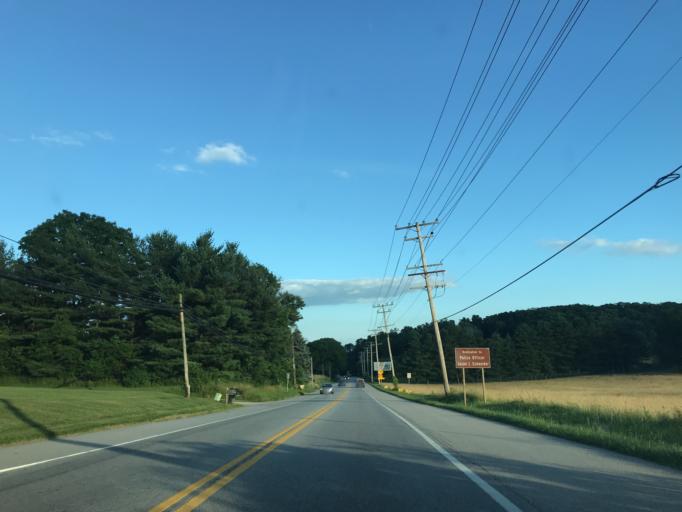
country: US
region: Maryland
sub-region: Carroll County
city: Manchester
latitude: 39.6472
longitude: -76.8770
